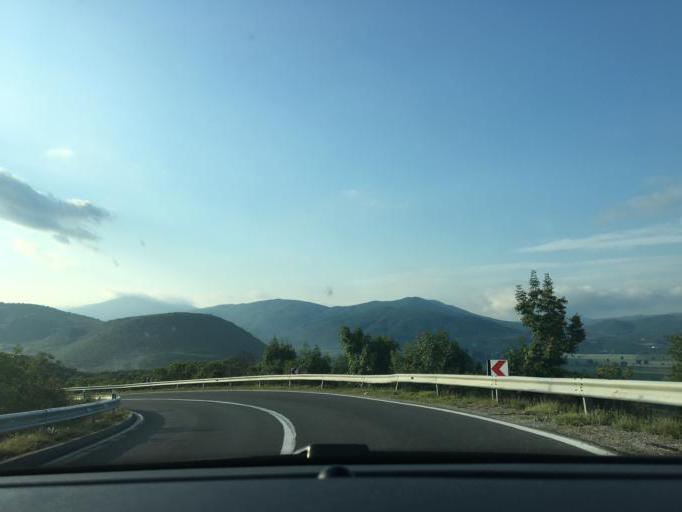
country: MK
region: Valandovo
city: Valandovo
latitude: 41.3219
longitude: 22.5962
